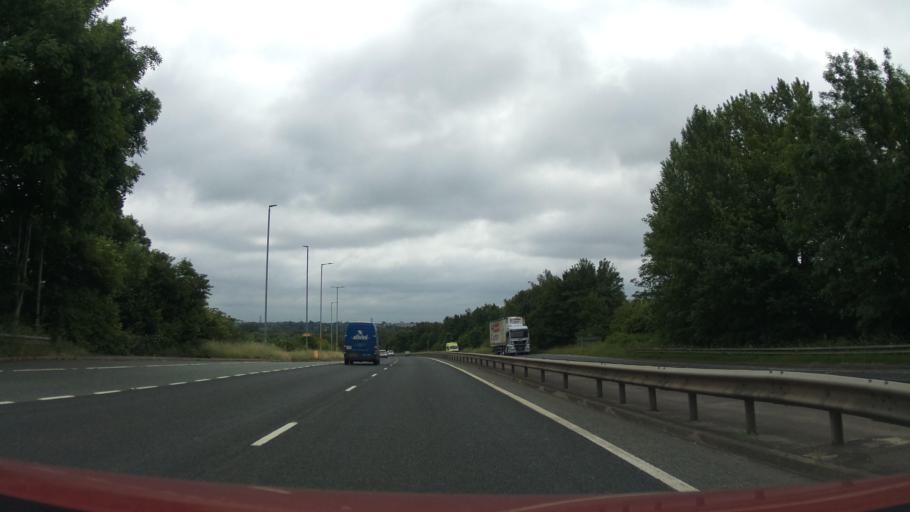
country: GB
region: England
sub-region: Leicestershire
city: Glenfield
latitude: 52.6639
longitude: -1.2238
